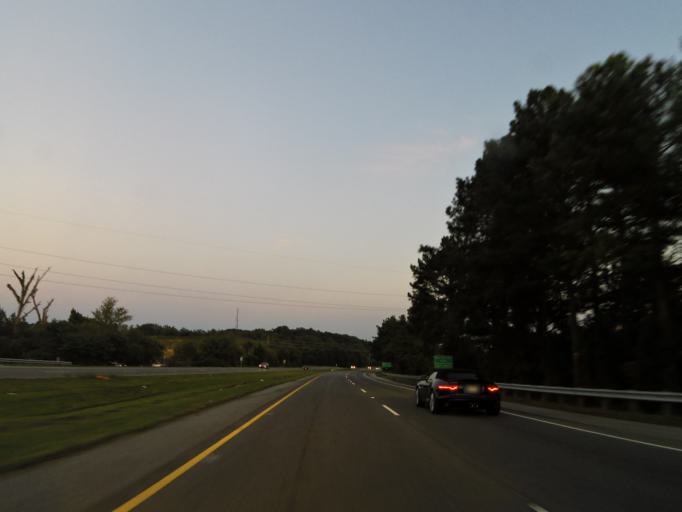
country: US
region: Tennessee
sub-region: Knox County
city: Farragut
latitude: 35.9515
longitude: -84.1591
